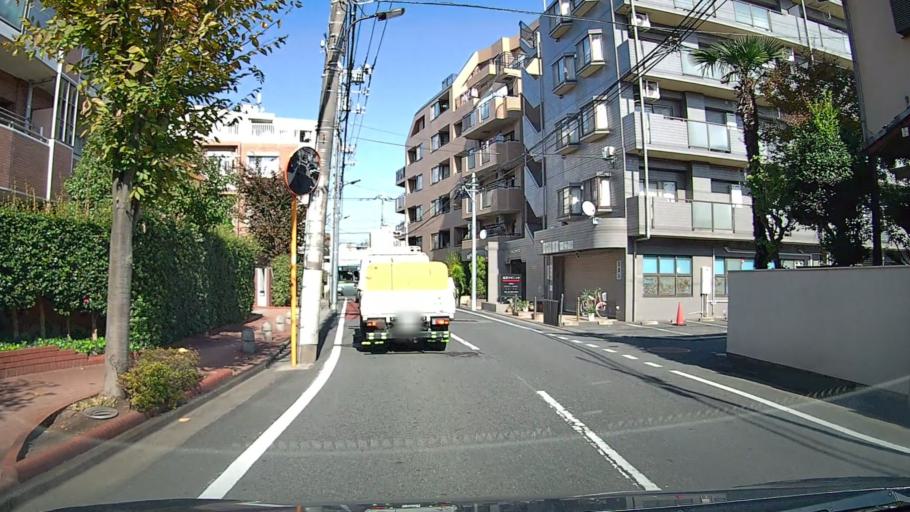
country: JP
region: Tokyo
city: Musashino
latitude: 35.7353
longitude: 139.5765
